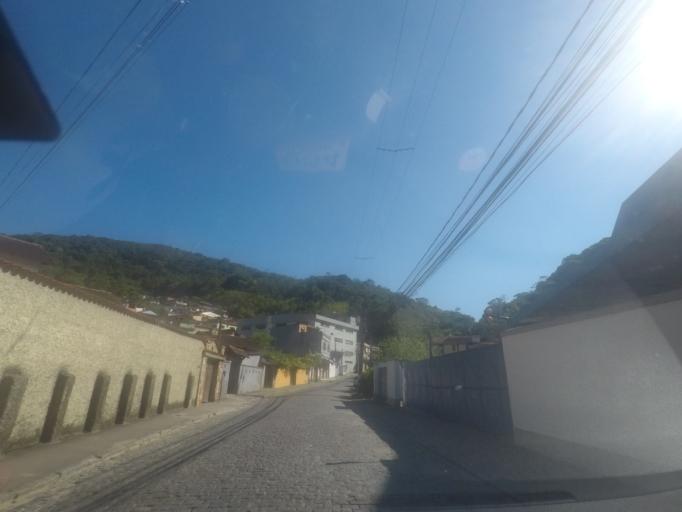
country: BR
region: Rio de Janeiro
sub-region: Petropolis
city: Petropolis
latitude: -22.5372
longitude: -43.1996
